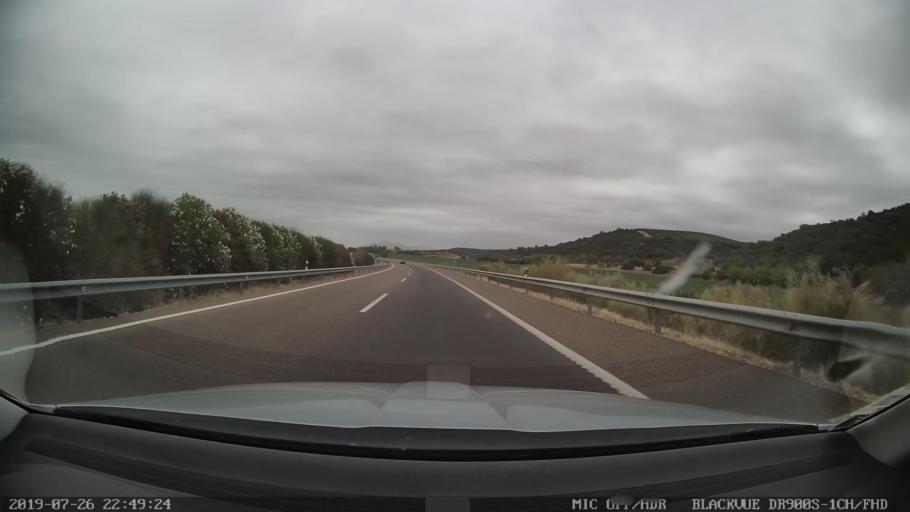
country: ES
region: Extremadura
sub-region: Provincia de Badajoz
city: Torremayor
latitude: 38.8595
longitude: -6.5675
